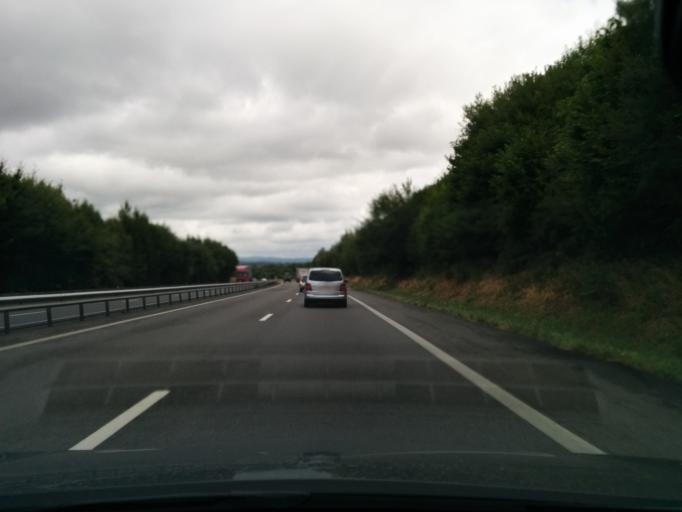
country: FR
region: Limousin
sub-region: Departement de la Correze
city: Uzerche
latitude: 45.4715
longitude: 1.5210
